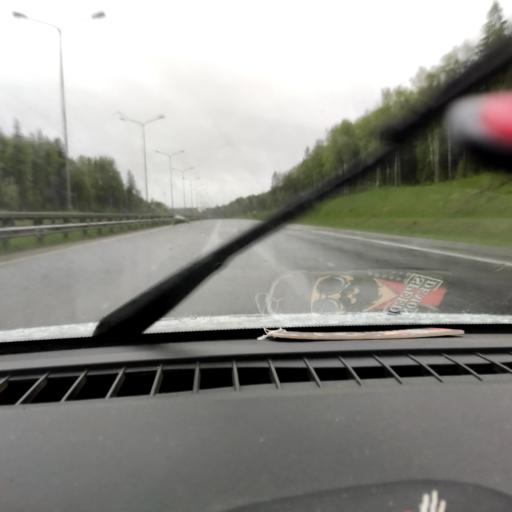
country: RU
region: Perm
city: Zvezdnyy
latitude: 57.7565
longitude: 56.3330
